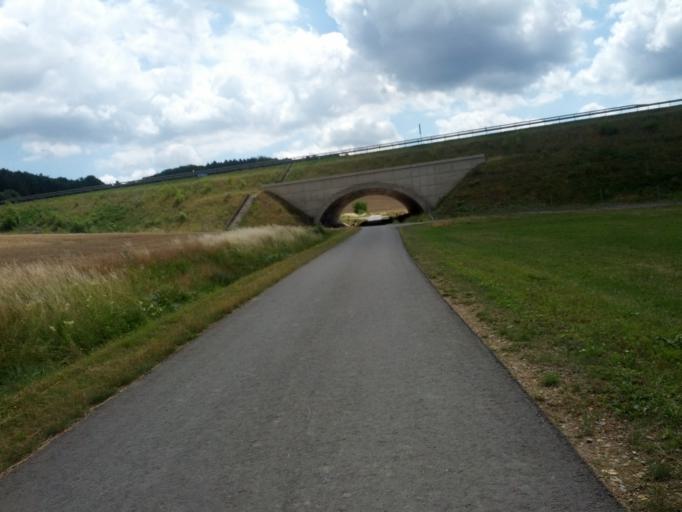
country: DE
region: Thuringia
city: Krauthausen
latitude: 51.0073
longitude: 10.2744
